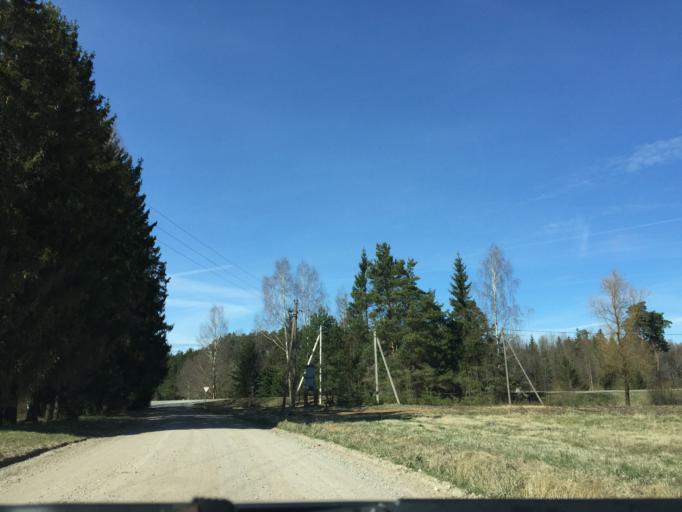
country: LT
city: Kursenai
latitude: 55.8341
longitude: 23.0422
